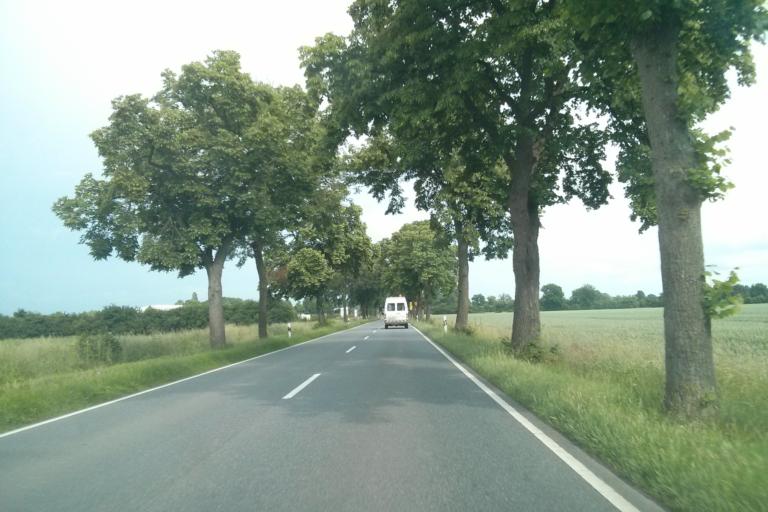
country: DE
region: Lower Saxony
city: Ahsen-Oetzen
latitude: 52.9652
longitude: 9.0538
